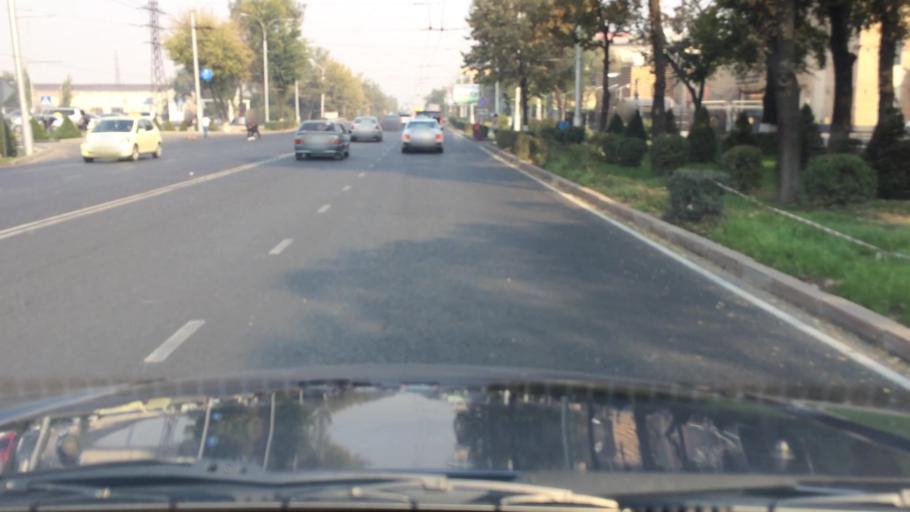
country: KG
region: Chuy
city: Bishkek
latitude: 42.8549
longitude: 74.5867
